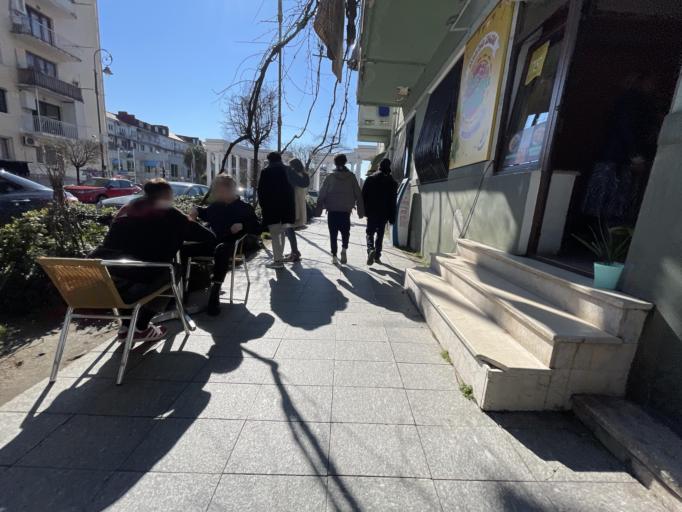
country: GE
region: Ajaria
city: Batumi
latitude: 41.6481
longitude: 41.6304
